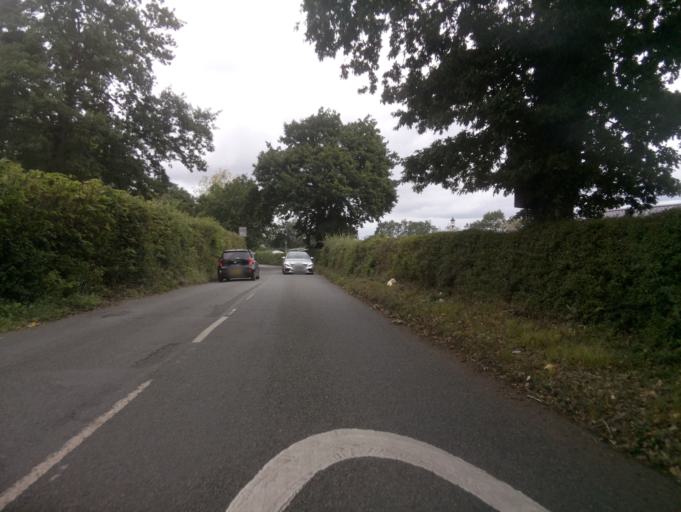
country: GB
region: England
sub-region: Devon
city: Starcross
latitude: 50.6034
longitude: -3.4467
